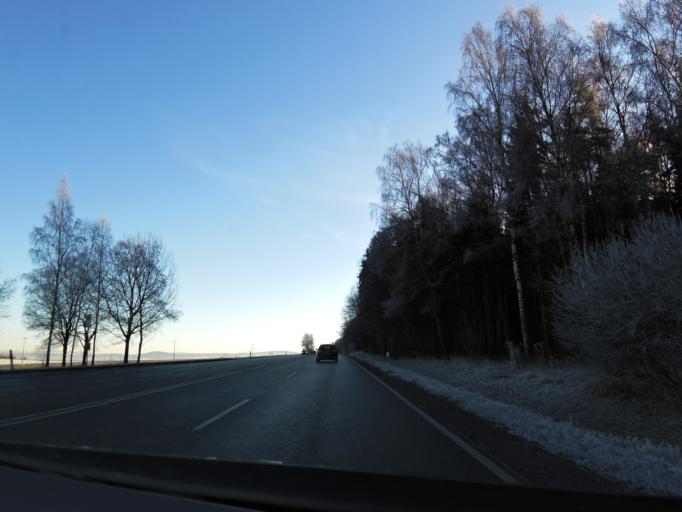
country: DE
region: Bavaria
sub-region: Upper Palatinate
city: Waldershof
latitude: 50.0132
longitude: 12.0508
